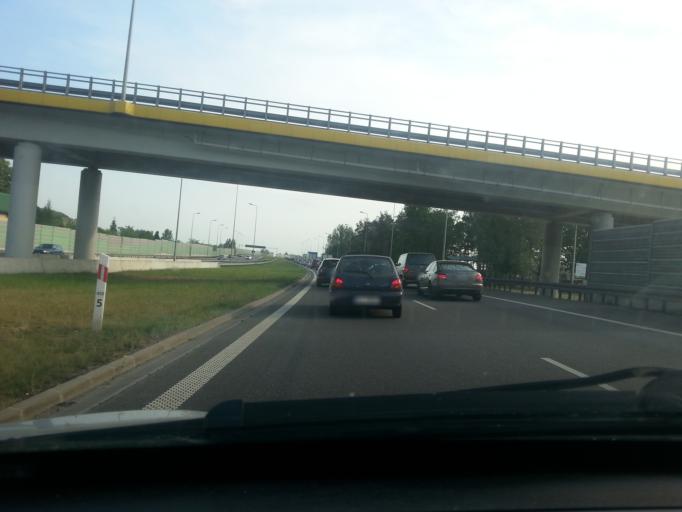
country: PL
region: Masovian Voivodeship
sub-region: Powiat warszawski zachodni
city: Ozarow Mazowiecki
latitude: 52.1851
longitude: 20.7742
